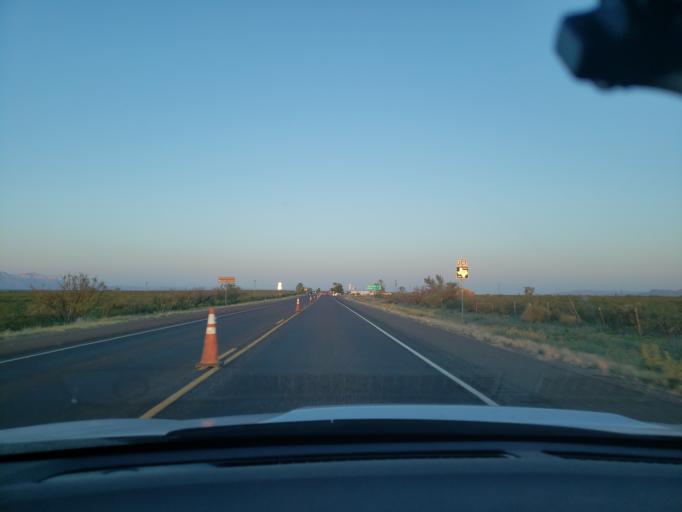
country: US
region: Texas
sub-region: Hudspeth County
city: Sierra Blanca
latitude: 31.7620
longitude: -105.3711
